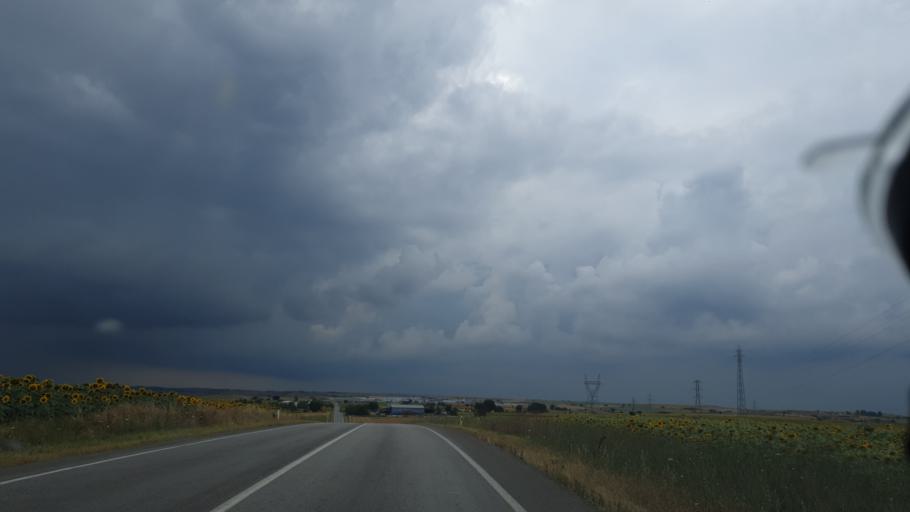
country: TR
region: Tekirdag
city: Hayrabolu
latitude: 41.2181
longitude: 27.0858
